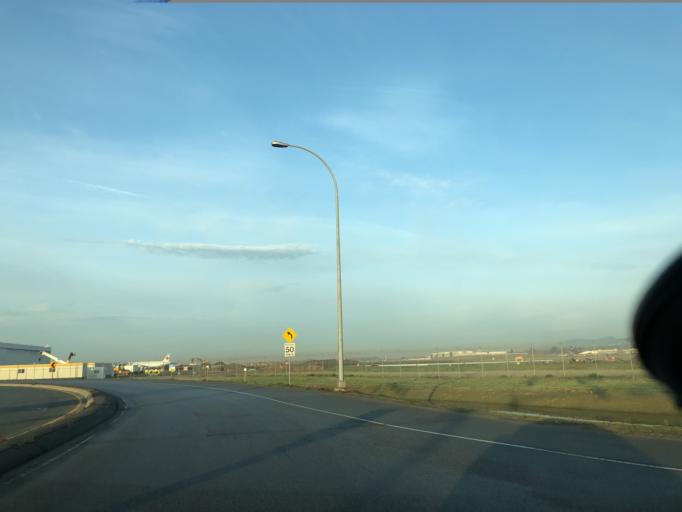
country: CA
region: British Columbia
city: Richmond
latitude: 49.1969
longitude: -123.1502
